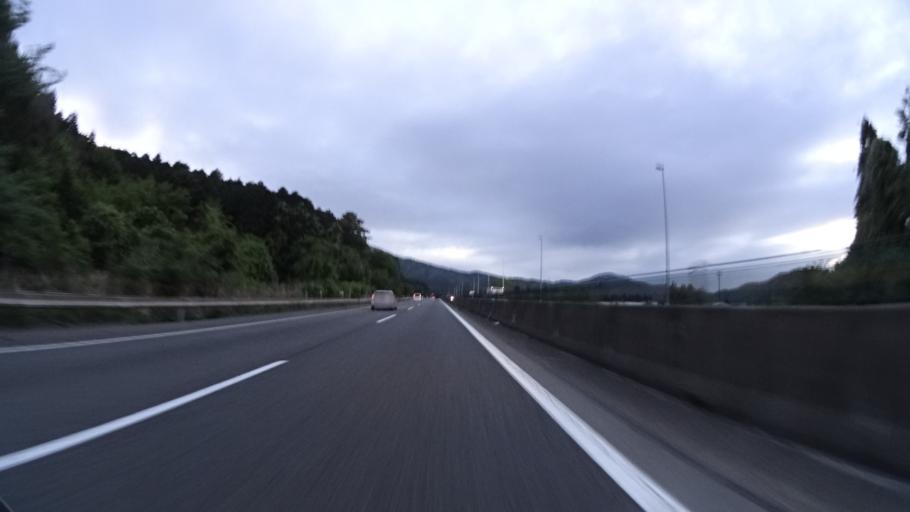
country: JP
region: Gifu
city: Tarui
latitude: 35.3422
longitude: 136.4079
